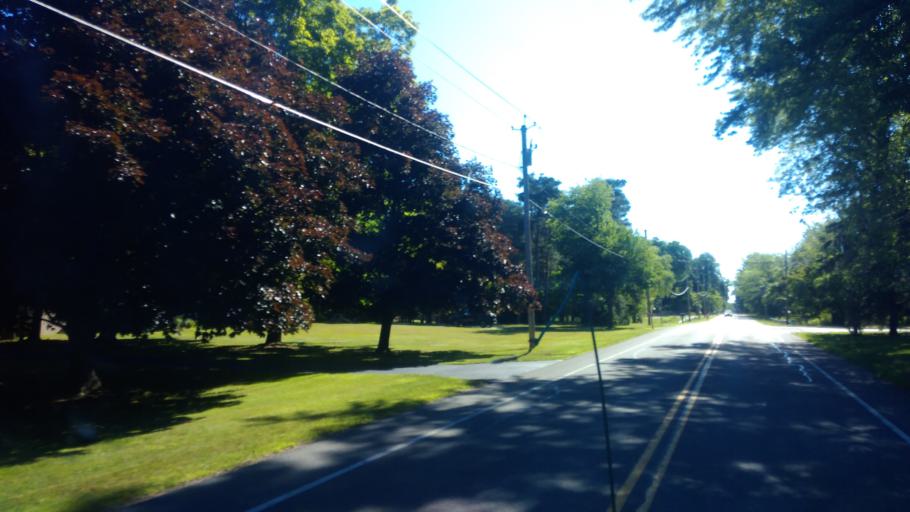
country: US
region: New York
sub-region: Monroe County
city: Webster
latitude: 43.2375
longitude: -77.4624
